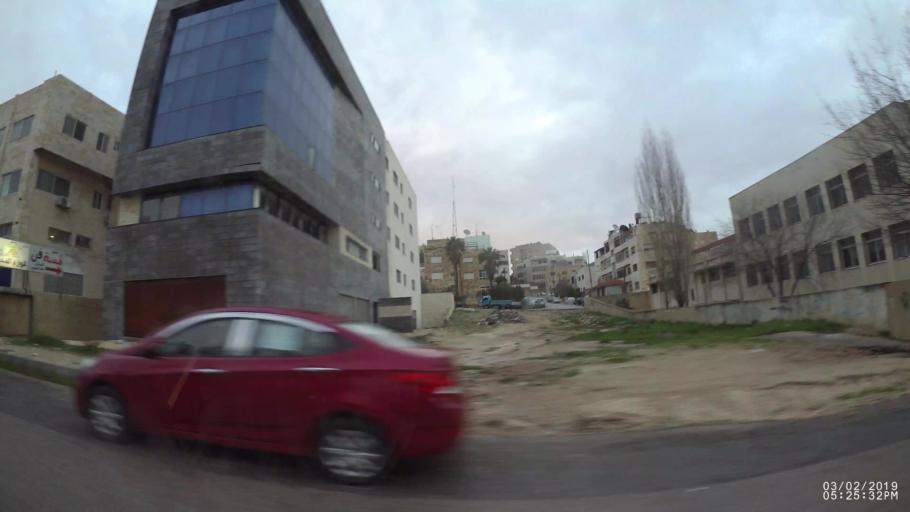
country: JO
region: Amman
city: Amman
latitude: 31.9830
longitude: 35.9106
